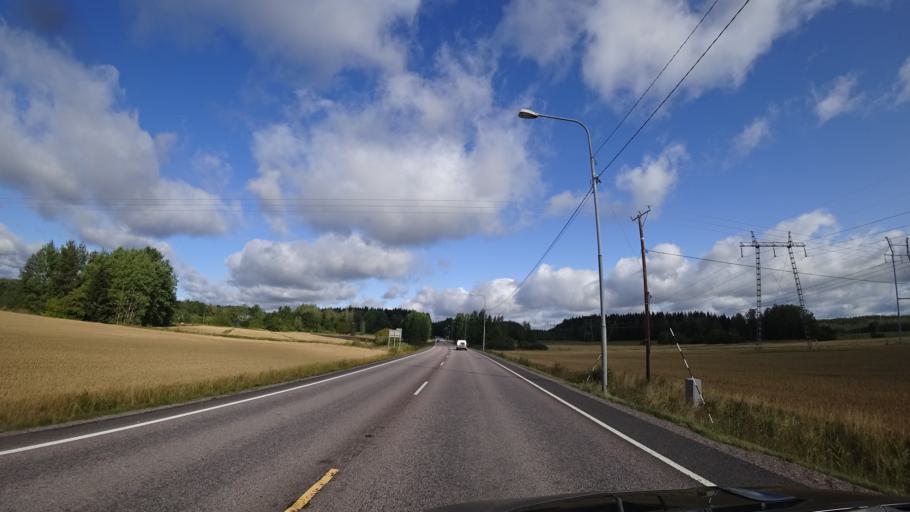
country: FI
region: Uusimaa
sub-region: Helsinki
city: Hyvinge
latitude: 60.5271
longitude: 24.9238
